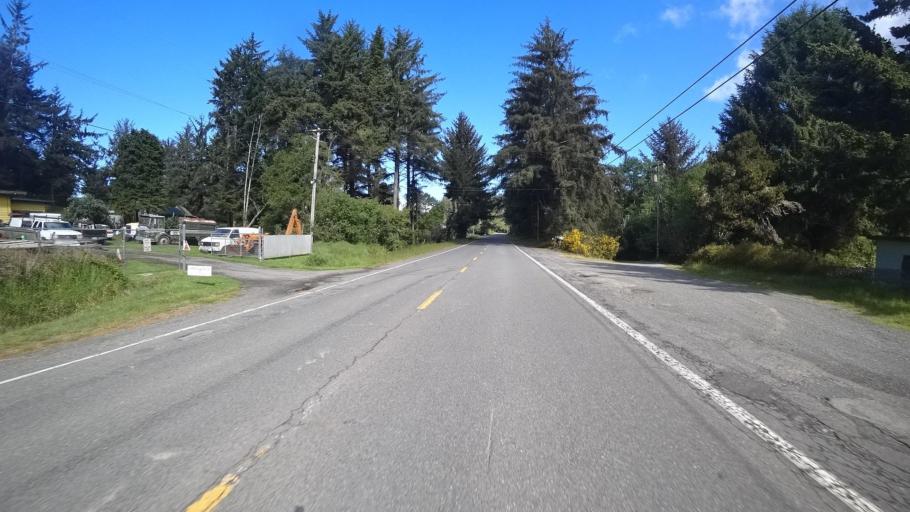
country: US
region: California
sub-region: Humboldt County
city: McKinleyville
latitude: 40.9857
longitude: -124.1062
